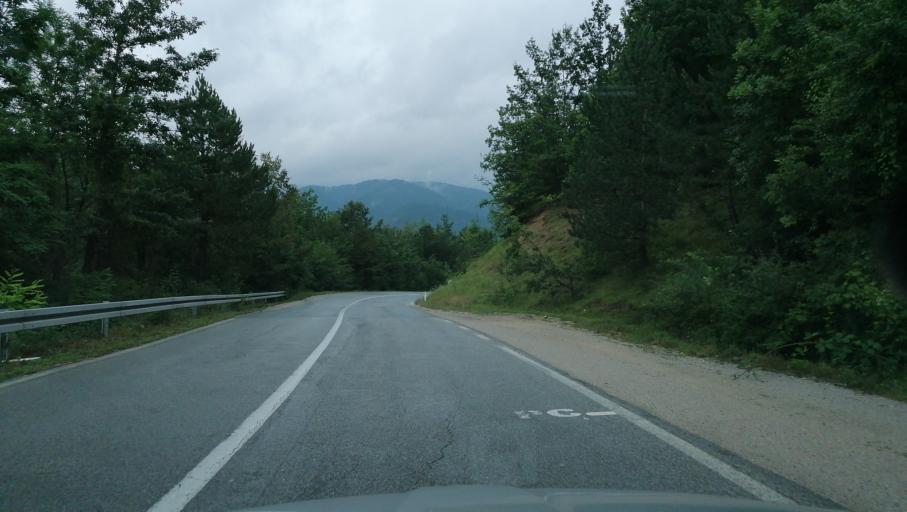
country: RS
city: Durici
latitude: 43.8083
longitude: 19.5097
